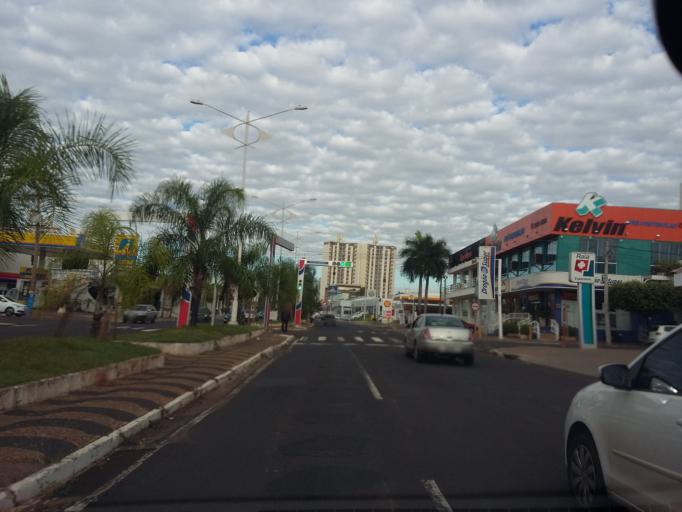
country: BR
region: Sao Paulo
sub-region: Sao Jose Do Rio Preto
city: Sao Jose do Rio Preto
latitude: -20.8169
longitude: -49.3941
